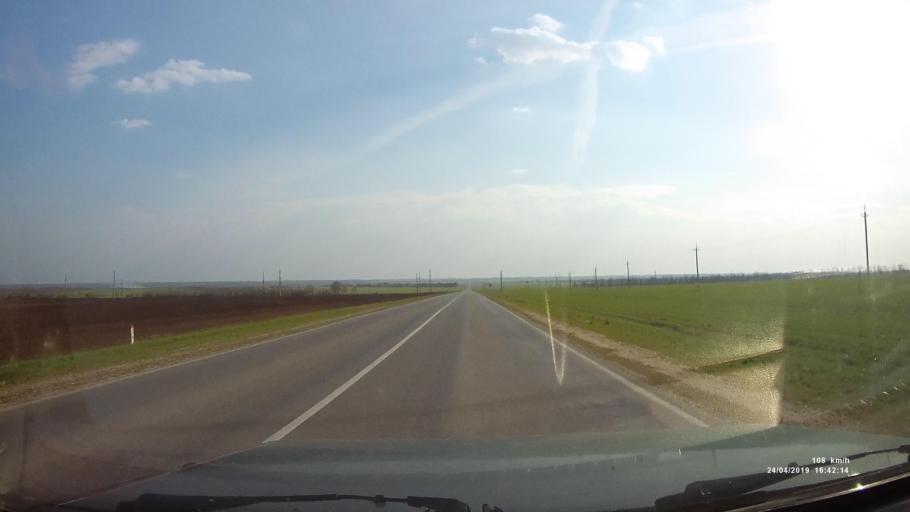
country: RU
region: Rostov
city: Gundorovskiy
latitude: 46.8099
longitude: 41.8568
